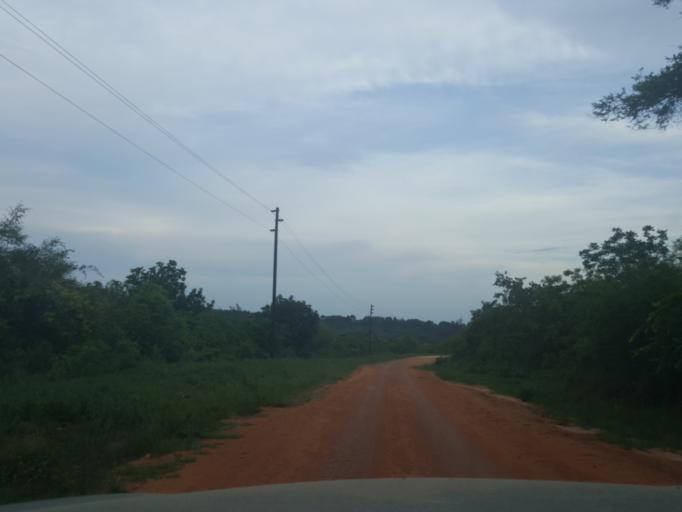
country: ZA
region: Limpopo
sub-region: Mopani District Municipality
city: Hoedspruit
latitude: -24.5959
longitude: 30.9275
